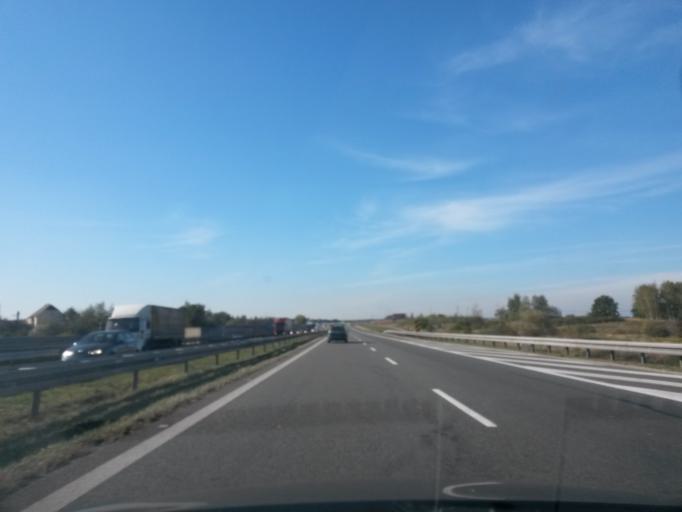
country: PL
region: Opole Voivodeship
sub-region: Powiat krapkowicki
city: Krapkowice
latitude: 50.5183
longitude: 17.9492
